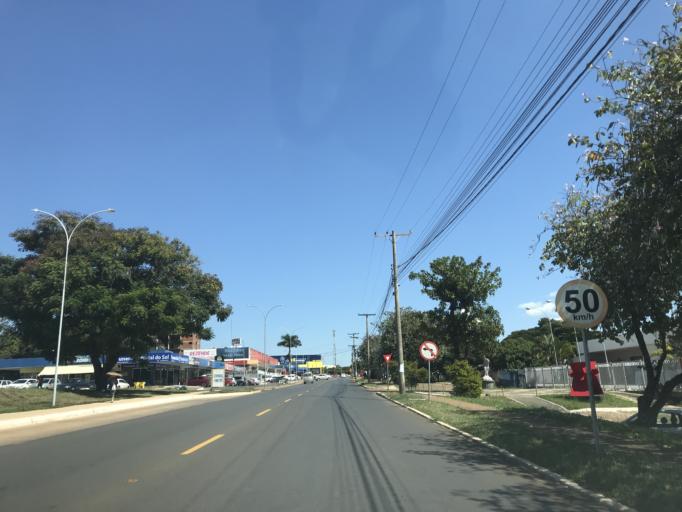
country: BR
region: Federal District
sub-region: Brasilia
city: Brasilia
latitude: -15.6494
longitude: -47.7864
